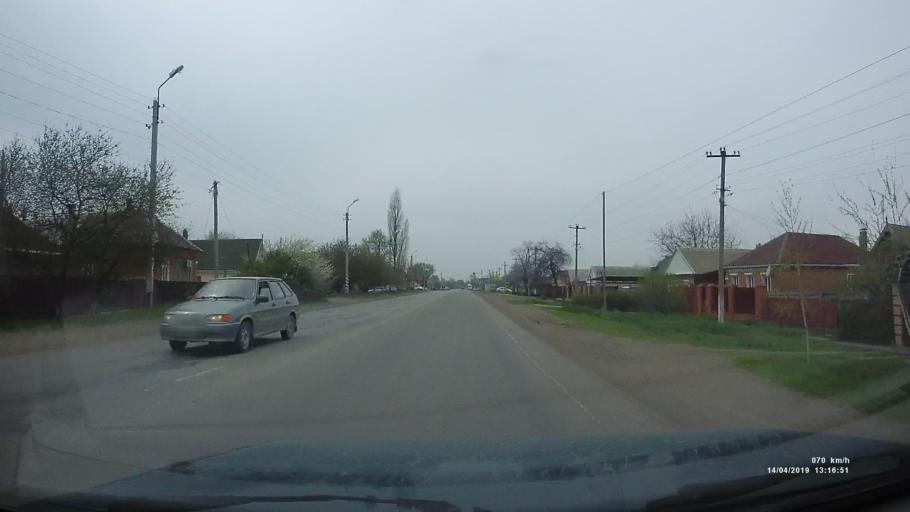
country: RU
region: Rostov
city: Kuleshovka
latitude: 47.0792
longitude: 39.5745
